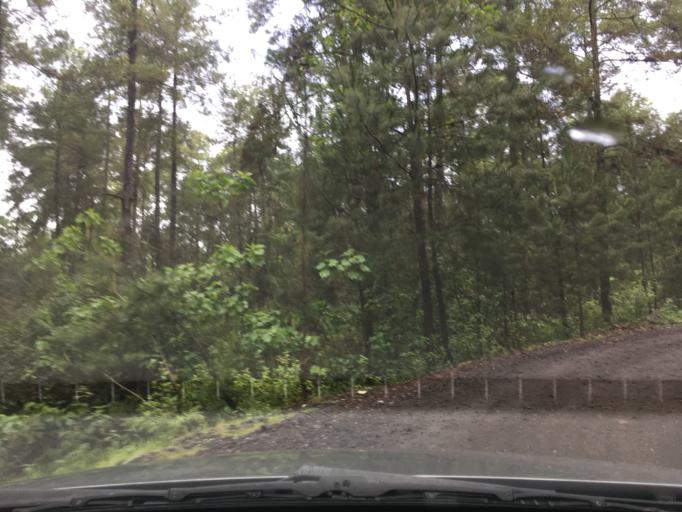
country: MX
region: Michoacan
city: Nuevo San Juan Parangaricutiro
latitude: 19.4507
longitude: -102.1866
